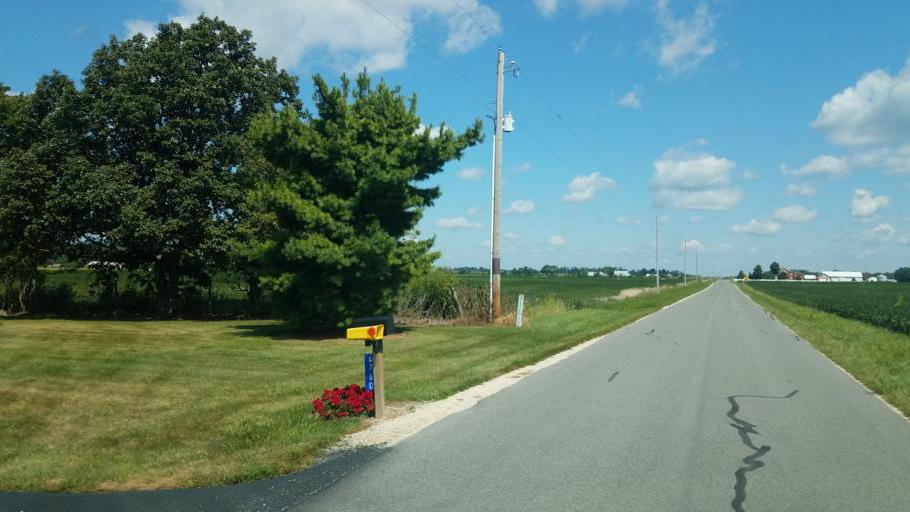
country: US
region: Ohio
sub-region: Wyandot County
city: Carey
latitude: 41.0249
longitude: -83.3244
